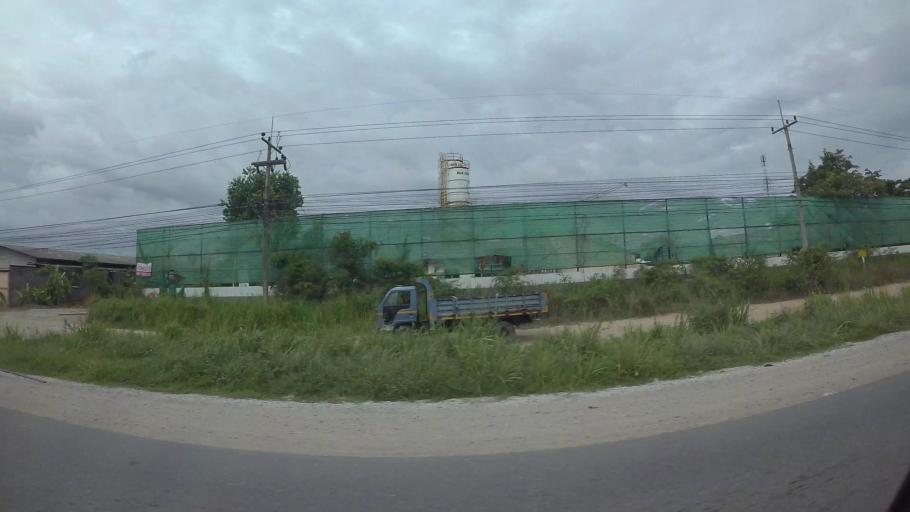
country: TH
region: Chon Buri
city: Bang Lamung
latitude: 12.9833
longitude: 100.9524
